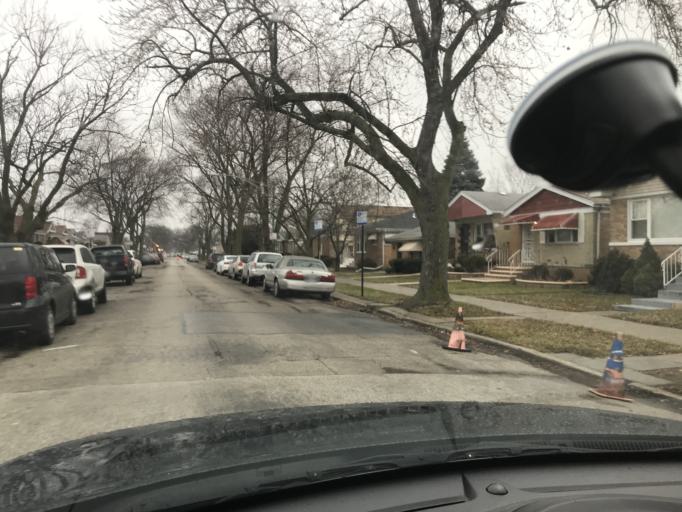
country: US
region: Illinois
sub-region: Cook County
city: Calumet Park
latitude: 41.7238
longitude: -87.6360
